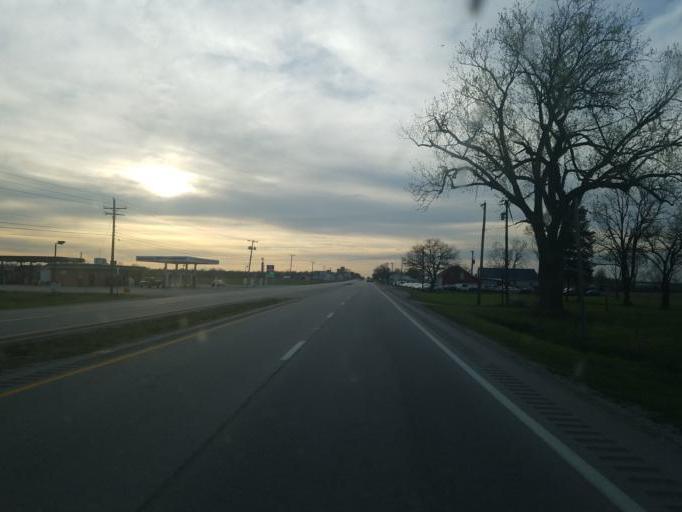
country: US
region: Ohio
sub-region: Sandusky County
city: Gibsonburg
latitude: 41.4229
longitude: -83.2949
